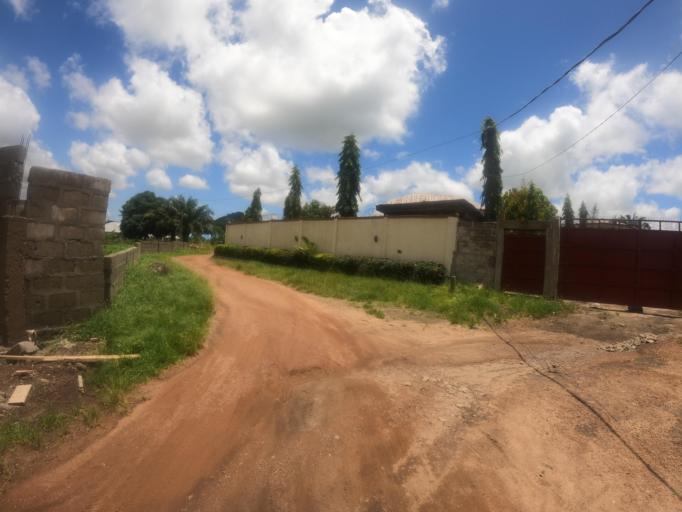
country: SL
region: Northern Province
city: Makeni
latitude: 8.8800
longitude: -12.0799
